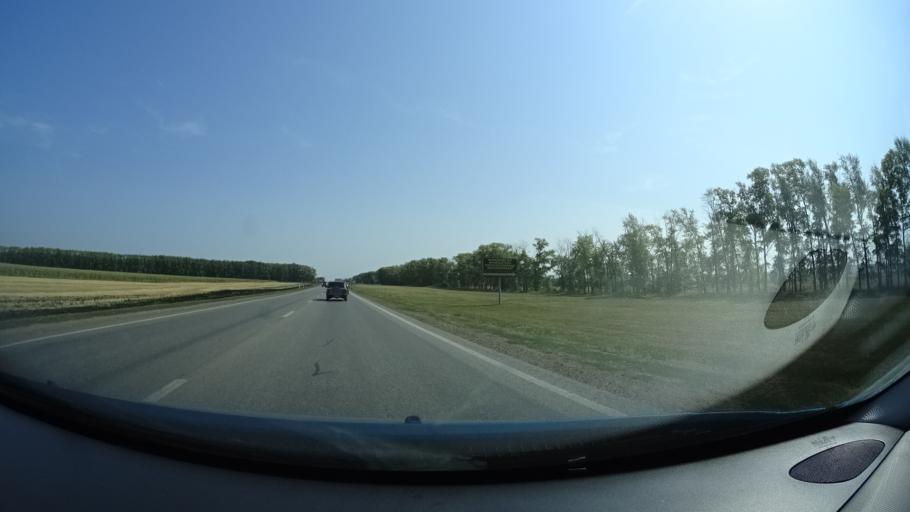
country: RU
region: Bashkortostan
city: Karmaskaly
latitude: 54.3852
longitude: 56.1679
